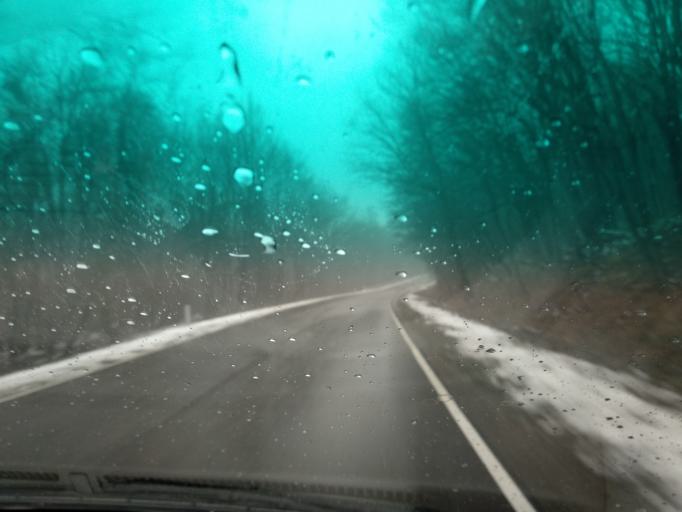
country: RU
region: Krasnodarskiy
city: Khadyzhensk
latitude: 44.2641
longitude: 39.3592
